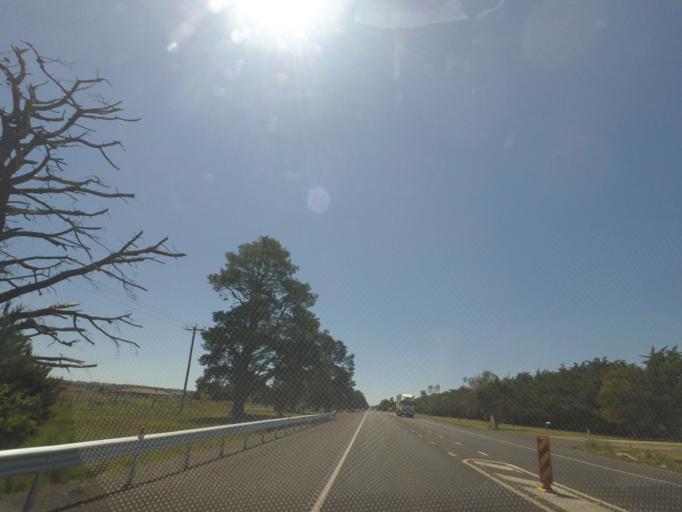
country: AU
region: Victoria
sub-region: Hume
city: Sunbury
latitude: -37.3784
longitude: 144.7463
